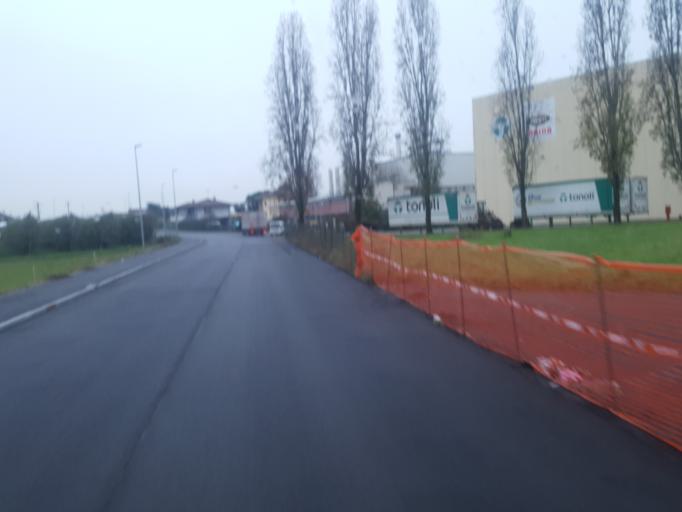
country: IT
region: Piedmont
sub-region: Provincia di Cuneo
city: Saluzzo
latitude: 44.6413
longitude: 7.5075
